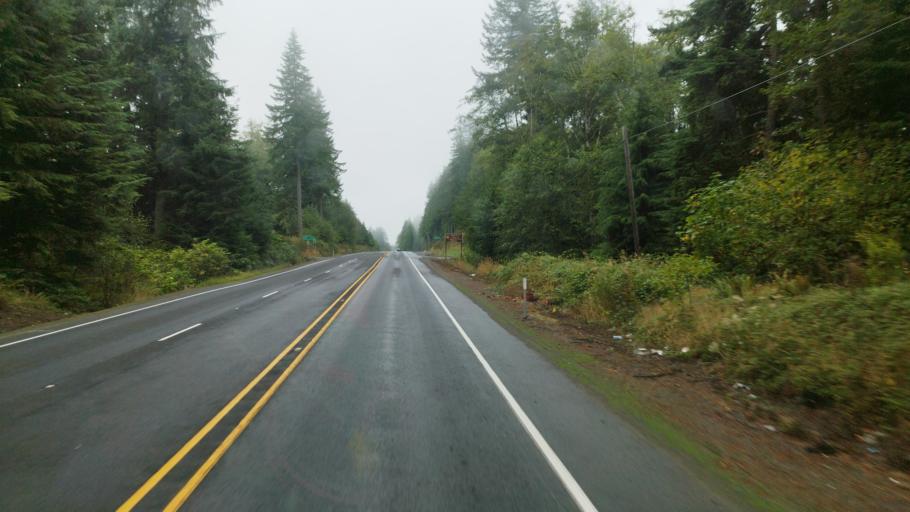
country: US
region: Washington
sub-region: Wahkiakum County
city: Cathlamet
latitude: 46.1691
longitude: -123.4551
